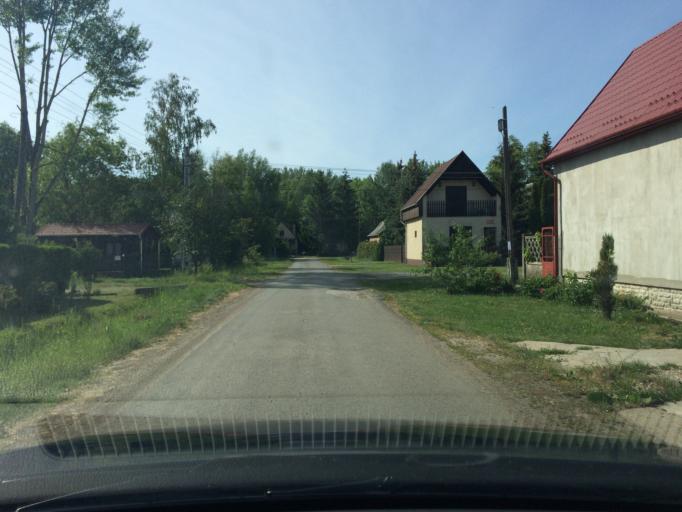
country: HU
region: Szabolcs-Szatmar-Bereg
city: Tiszavasvari
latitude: 47.9531
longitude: 21.3491
